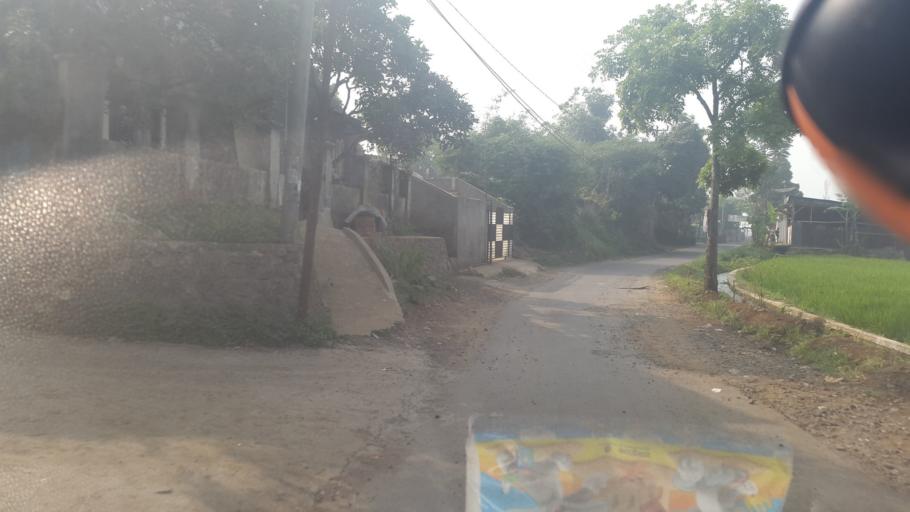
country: ID
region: West Java
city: Sukabumi
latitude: -6.9376
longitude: 106.9045
